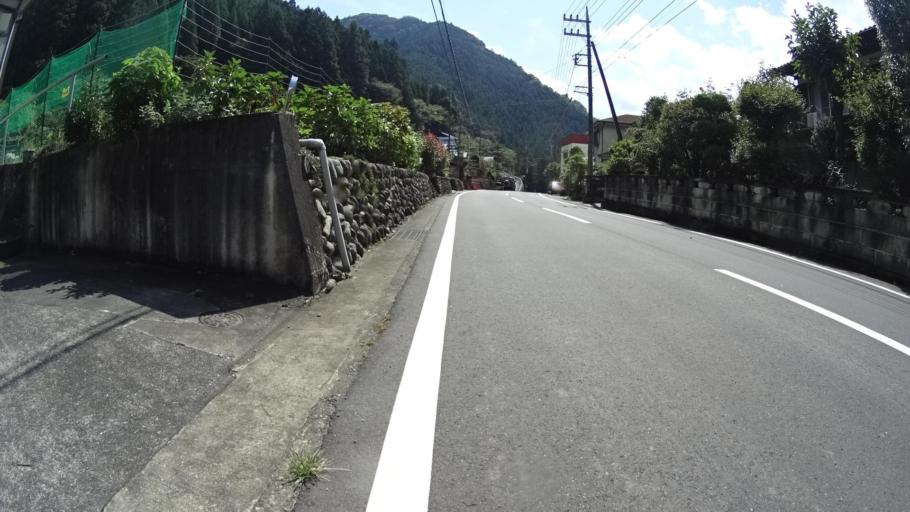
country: JP
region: Tokyo
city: Itsukaichi
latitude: 35.7375
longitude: 139.1438
